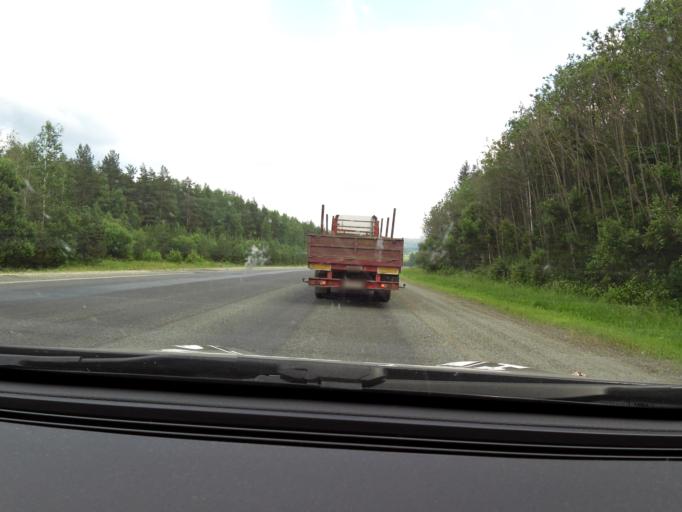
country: RU
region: Sverdlovsk
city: Ufimskiy
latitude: 56.7863
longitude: 58.3151
